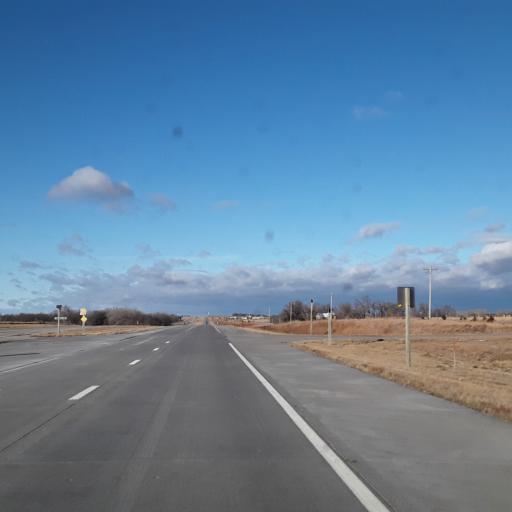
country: US
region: Kansas
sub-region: Republic County
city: Belleville
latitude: 39.8697
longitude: -97.6142
